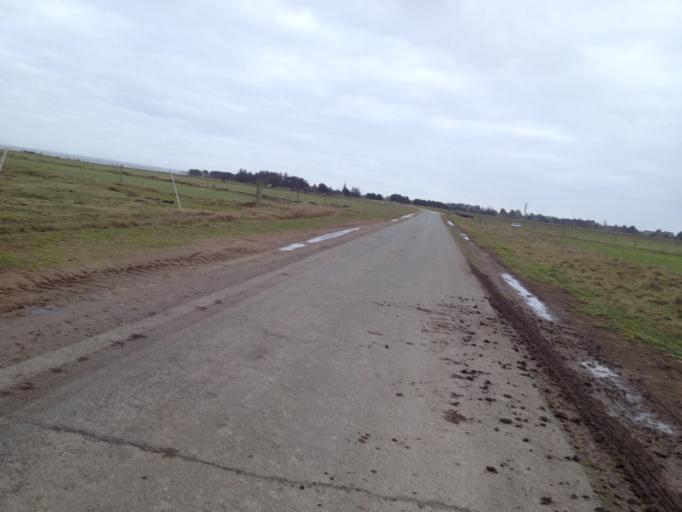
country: DE
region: Schleswig-Holstein
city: Nebel
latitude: 54.6607
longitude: 8.3484
